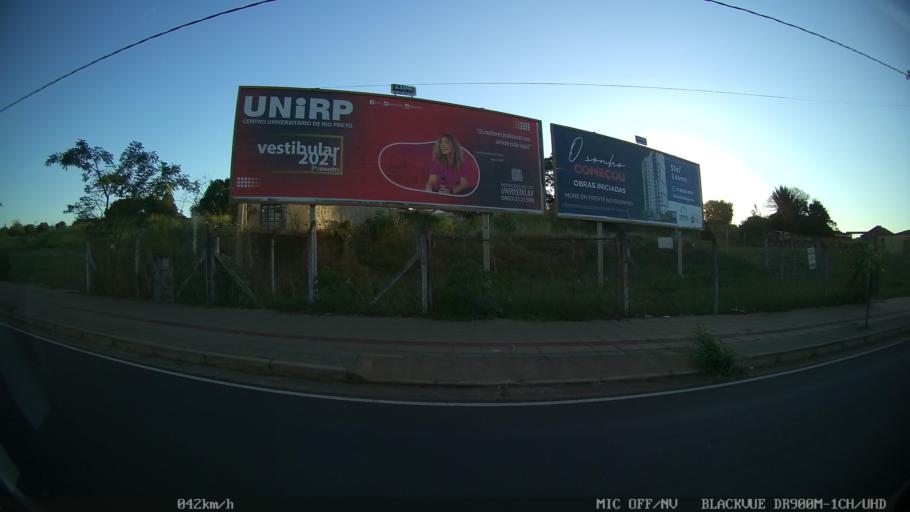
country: BR
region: Sao Paulo
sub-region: Sao Jose Do Rio Preto
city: Sao Jose do Rio Preto
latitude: -20.7935
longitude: -49.3770
